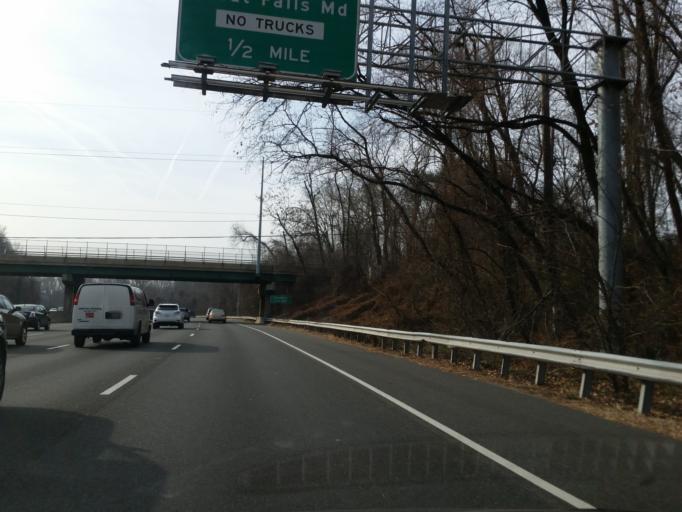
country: US
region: Maryland
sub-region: Montgomery County
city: Cabin John
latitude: 38.9821
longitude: -77.1716
